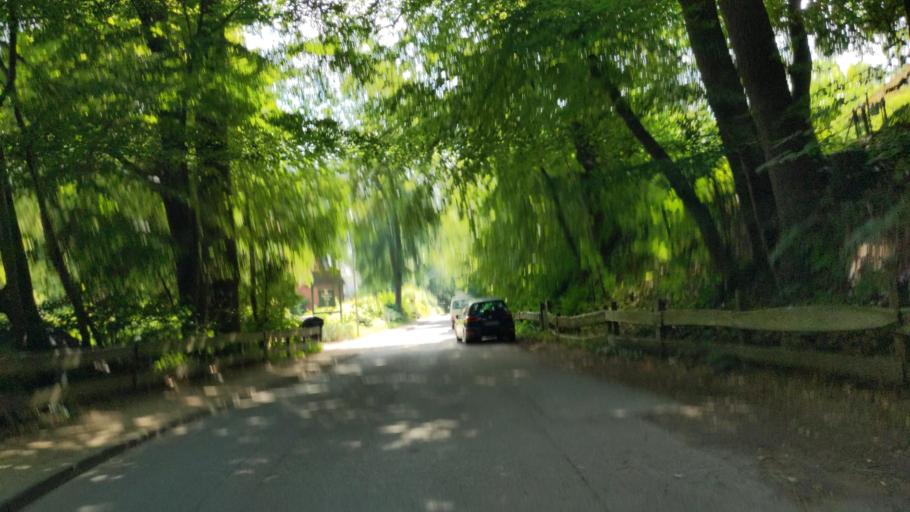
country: DE
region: Schleswig-Holstein
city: Susel
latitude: 54.0256
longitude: 10.7019
